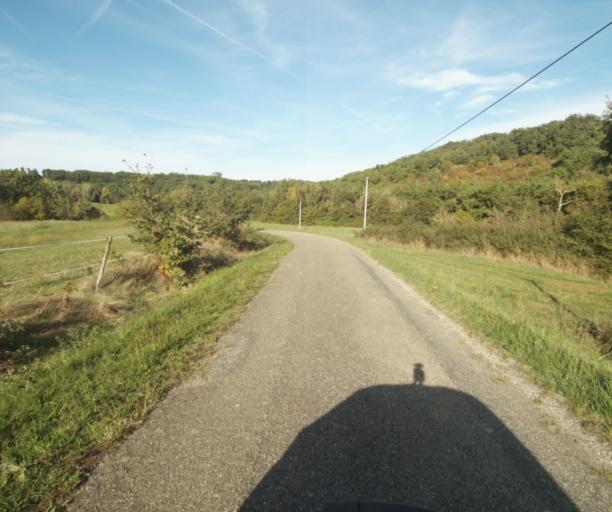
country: FR
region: Midi-Pyrenees
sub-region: Departement du Tarn-et-Garonne
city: Saint-Porquier
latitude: 43.9344
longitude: 1.1458
